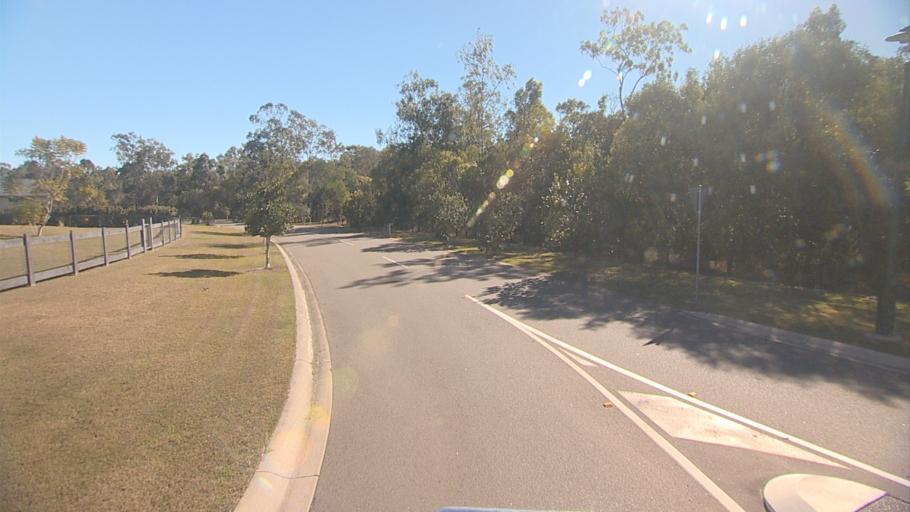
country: AU
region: Queensland
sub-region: Logan
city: North Maclean
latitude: -27.7526
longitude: 152.9663
